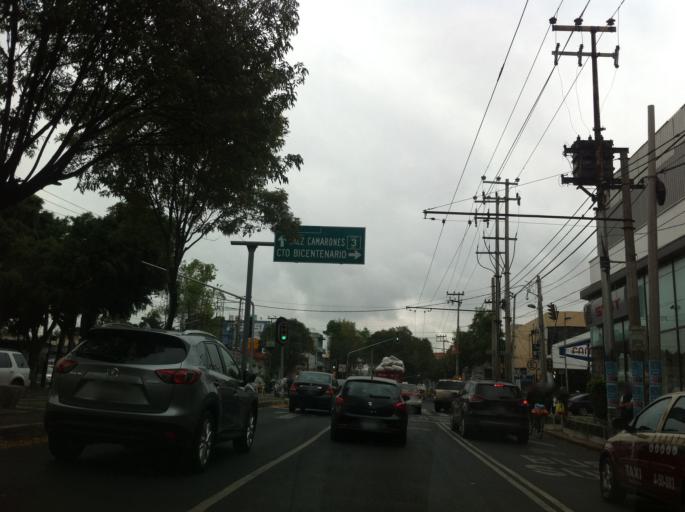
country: MX
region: Mexico City
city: Miguel Hidalgo
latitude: 19.4560
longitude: -99.1807
